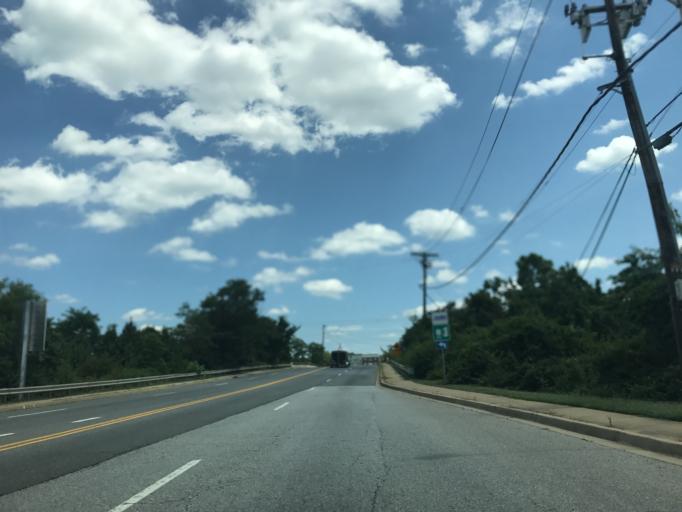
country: US
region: Maryland
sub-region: Prince George's County
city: Beltsville
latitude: 39.0627
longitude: -76.8871
